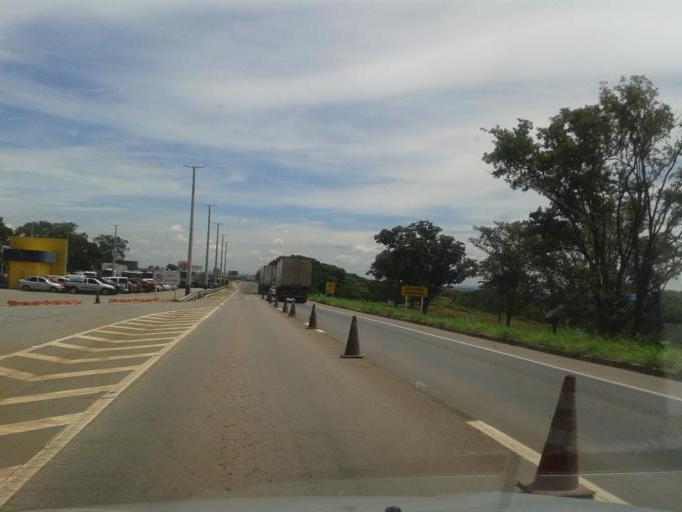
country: BR
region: Goias
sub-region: Hidrolandia
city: Hidrolandia
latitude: -16.9219
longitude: -49.2524
